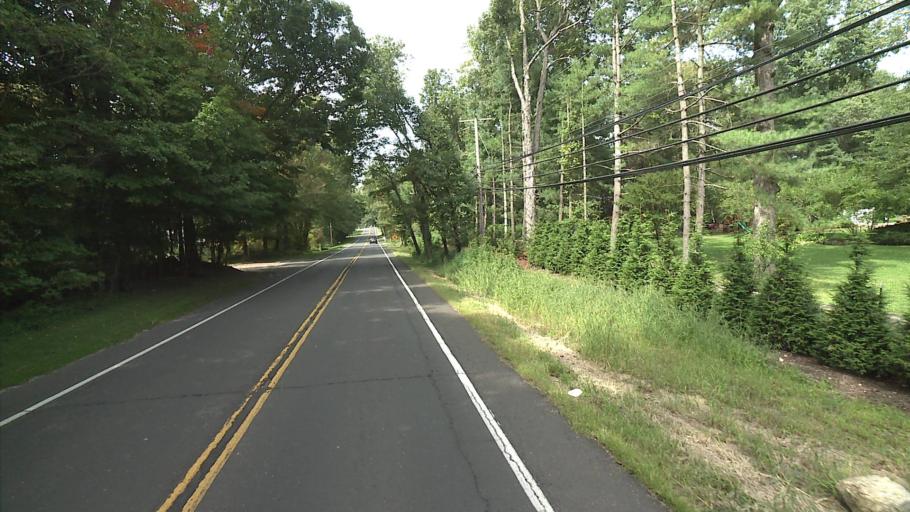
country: US
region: Connecticut
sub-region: Fairfield County
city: North Stamford
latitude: 41.1307
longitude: -73.5825
